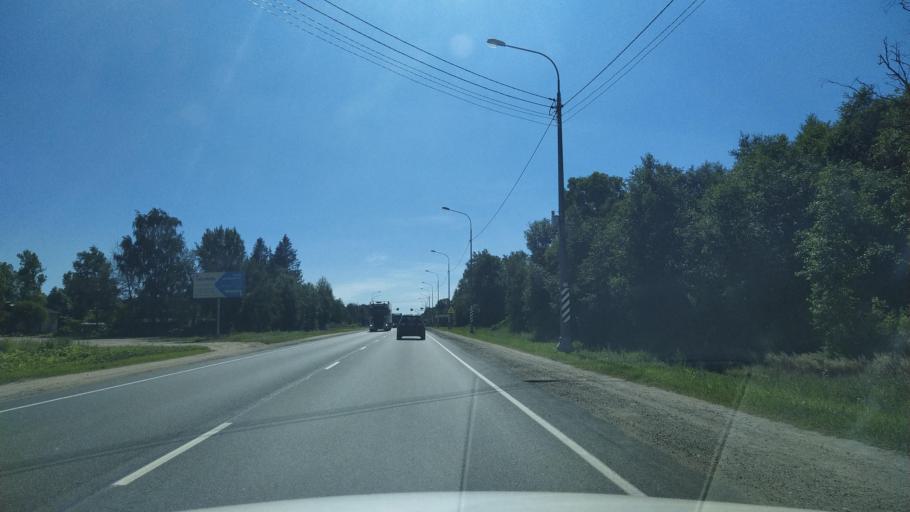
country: RU
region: Pskov
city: Pskov
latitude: 57.7880
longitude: 28.4105
